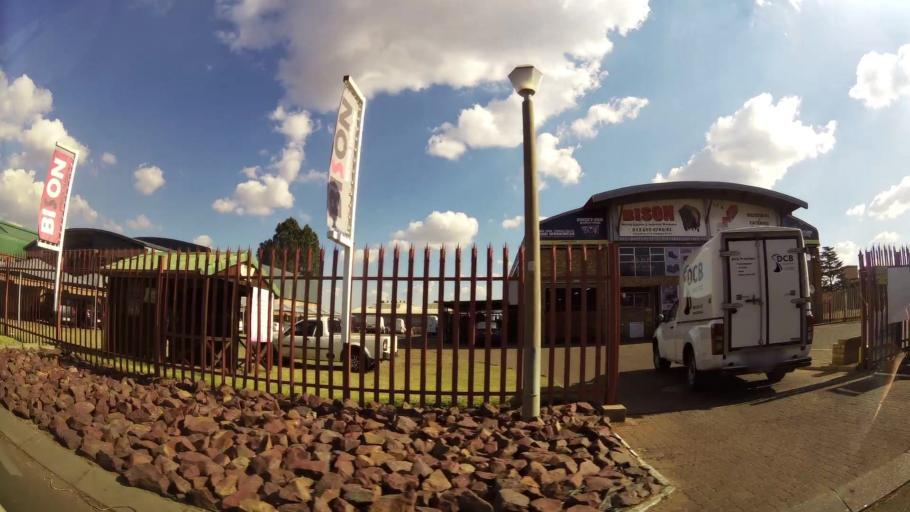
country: ZA
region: Mpumalanga
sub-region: Nkangala District Municipality
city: Witbank
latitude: -25.9023
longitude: 29.2297
